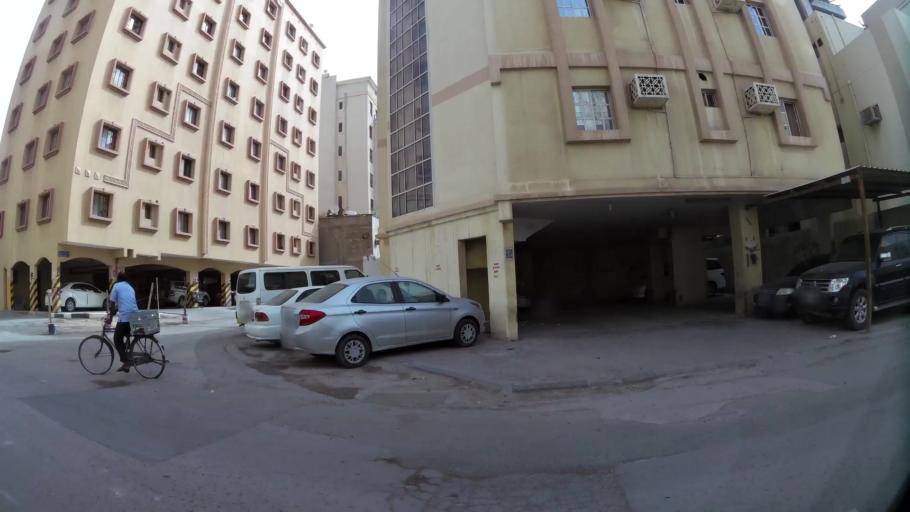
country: QA
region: Baladiyat ad Dawhah
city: Doha
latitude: 25.2780
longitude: 51.5499
